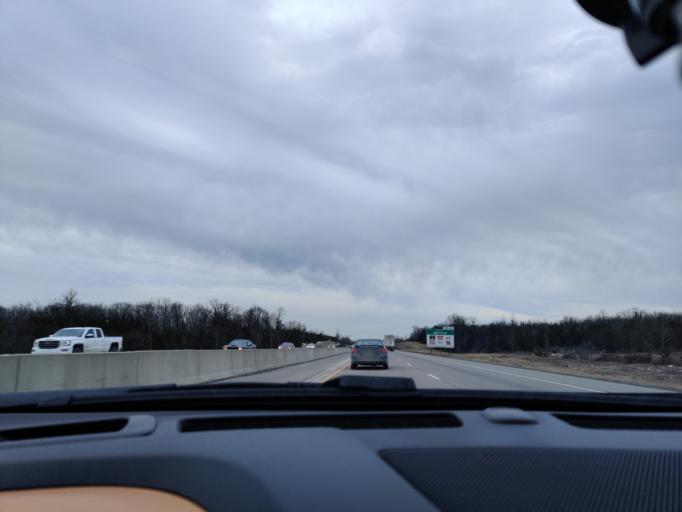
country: CA
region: Ontario
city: Deseronto
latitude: 44.2244
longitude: -77.2092
